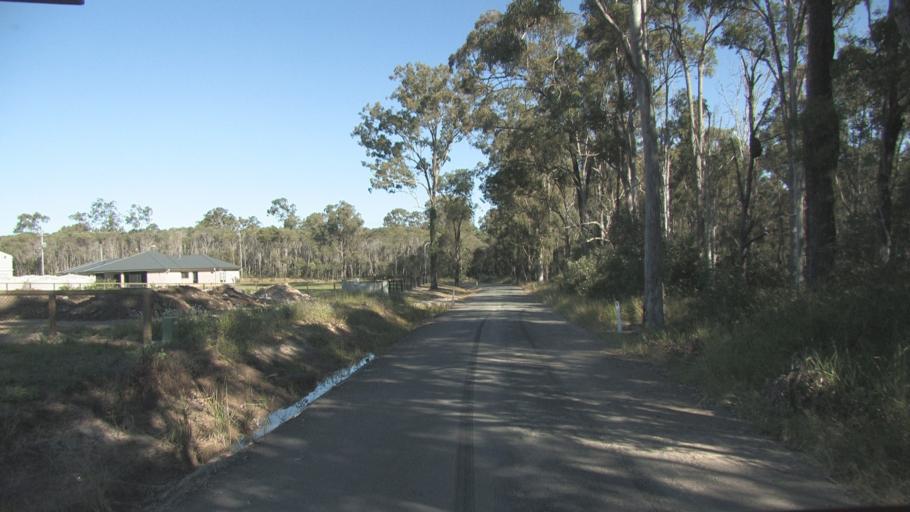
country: AU
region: Queensland
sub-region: Logan
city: Logan Reserve
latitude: -27.7535
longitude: 153.1381
